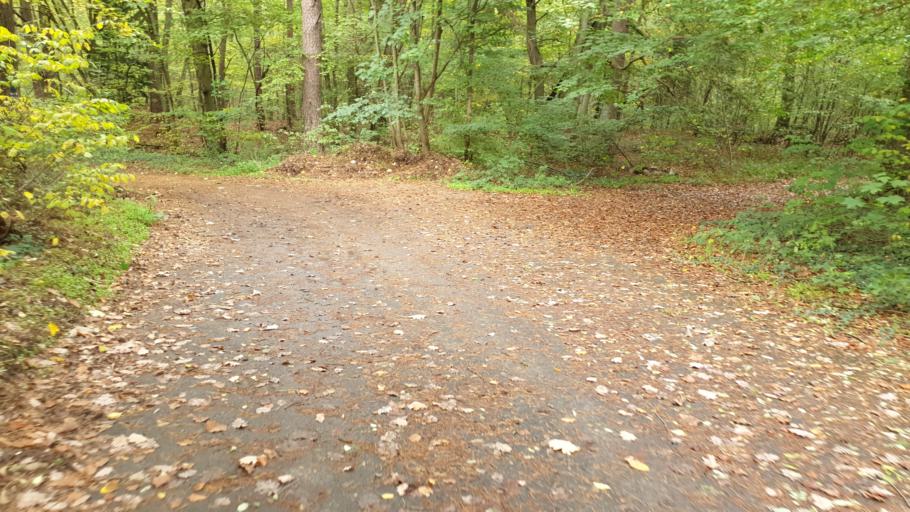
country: DE
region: Brandenburg
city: Chorin
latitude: 52.8930
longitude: 13.8790
